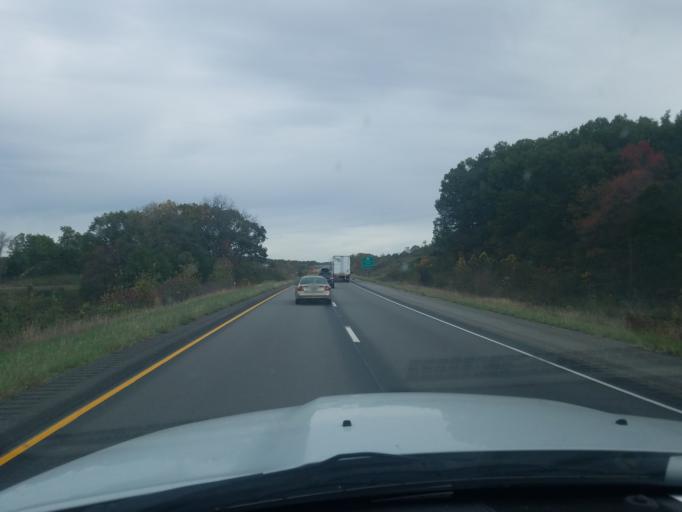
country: US
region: Indiana
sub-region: Dubois County
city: Ferdinand
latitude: 38.2066
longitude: -86.8867
